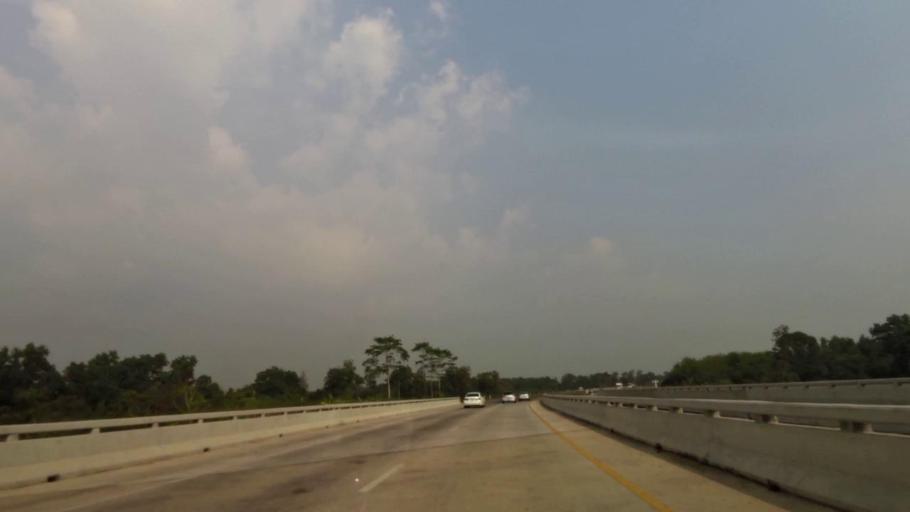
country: TH
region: Rayong
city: Klaeng
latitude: 12.8089
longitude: 101.6428
